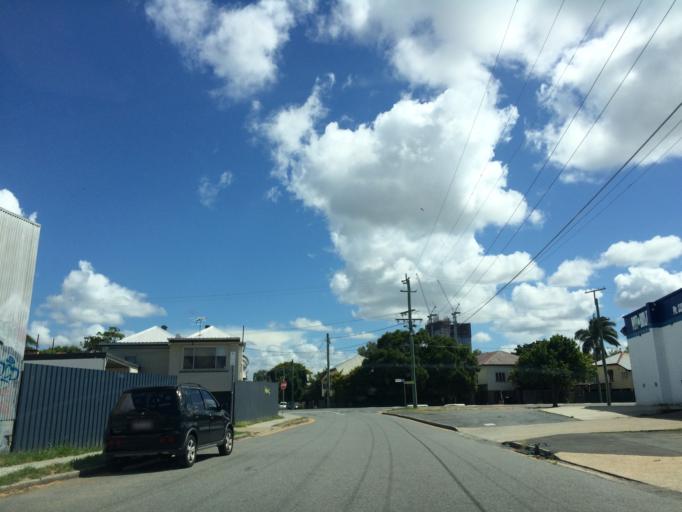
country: AU
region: Queensland
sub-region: Brisbane
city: Woolloongabba
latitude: -27.4915
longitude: 153.0437
